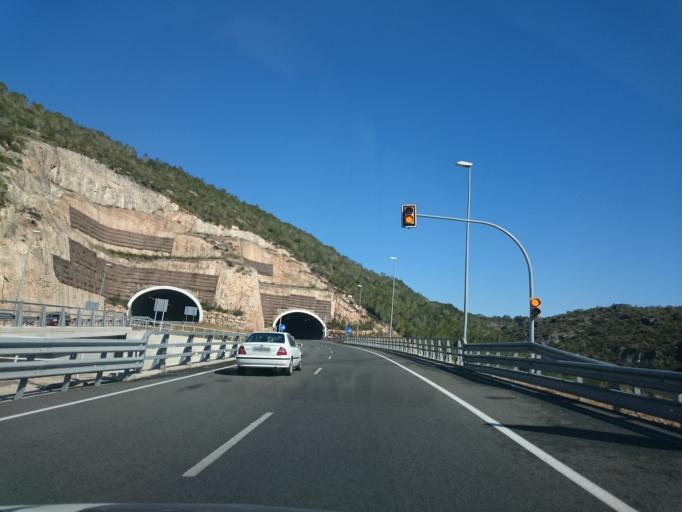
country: ES
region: Catalonia
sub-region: Provincia de Barcelona
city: Sant Pere de Ribes
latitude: 41.2975
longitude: 1.7269
